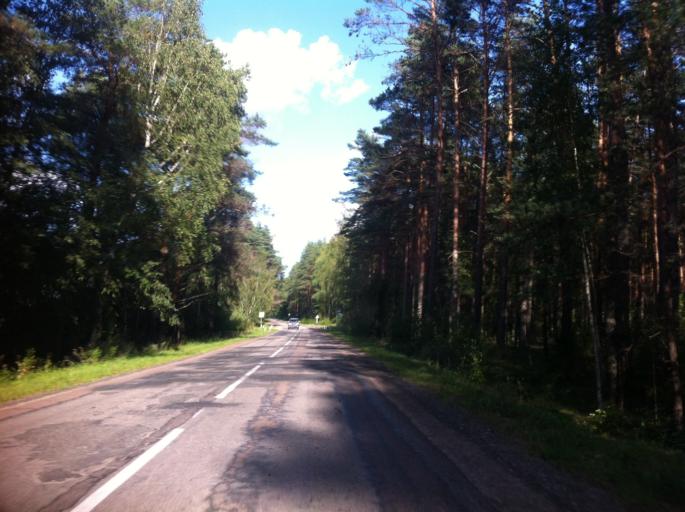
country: RU
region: Pskov
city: Izborsk
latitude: 57.8036
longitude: 27.7941
